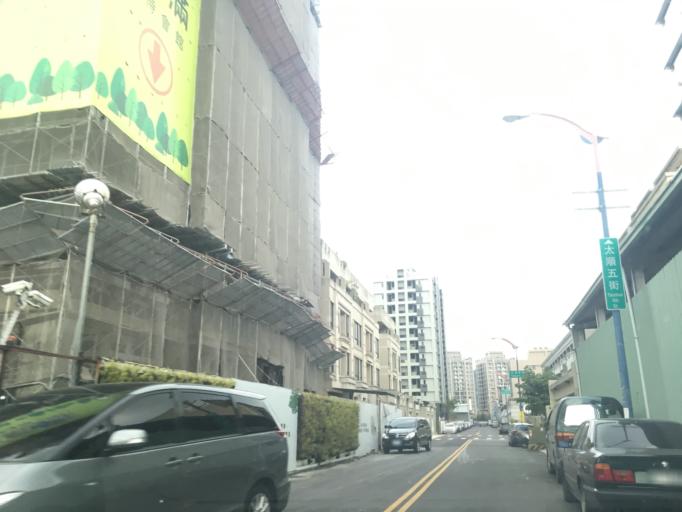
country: TW
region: Taiwan
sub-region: Taichung City
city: Taichung
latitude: 24.1614
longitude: 120.7226
